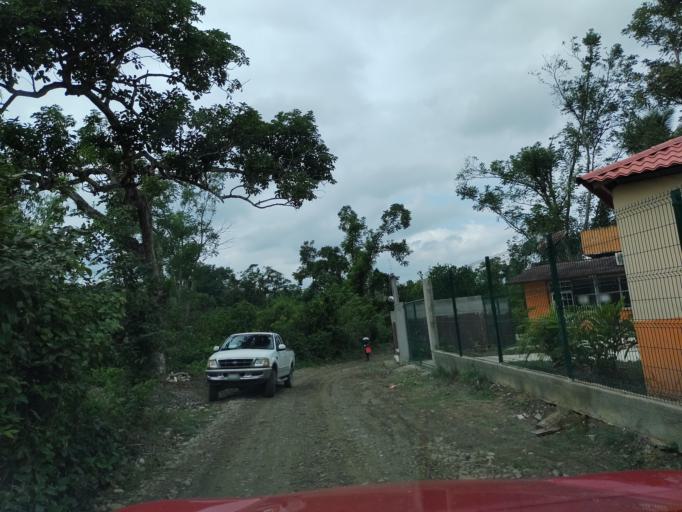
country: MX
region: Veracruz
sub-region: Coatzintla
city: Manuel Maria Contreras
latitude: 20.4446
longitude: -97.4422
